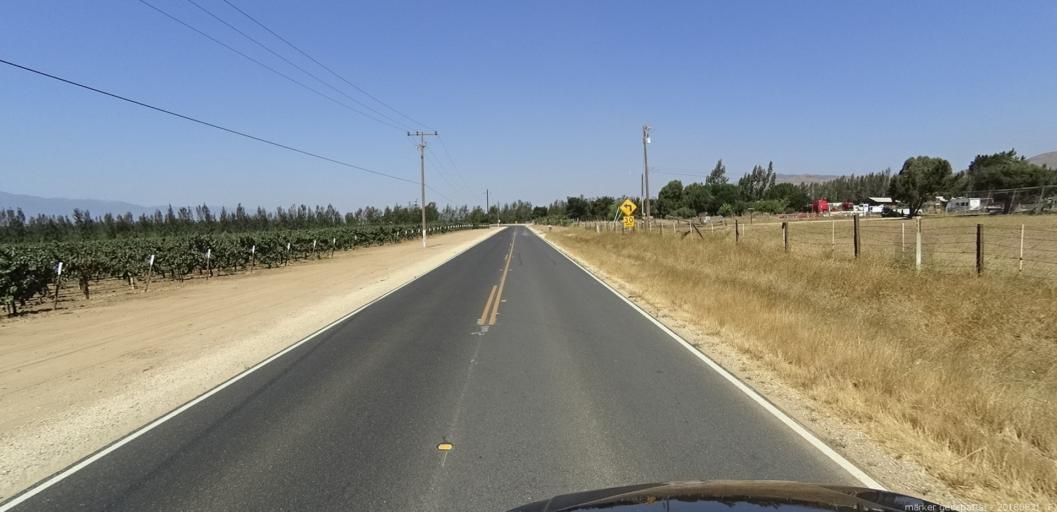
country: US
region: California
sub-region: Monterey County
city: Soledad
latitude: 36.4214
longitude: -121.2849
